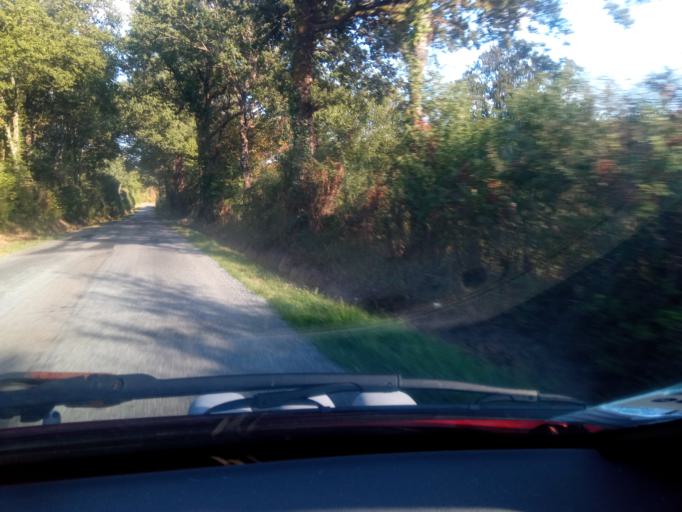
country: FR
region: Poitou-Charentes
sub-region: Departement de la Vienne
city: Availles-Limouzine
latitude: 46.1288
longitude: 0.7163
